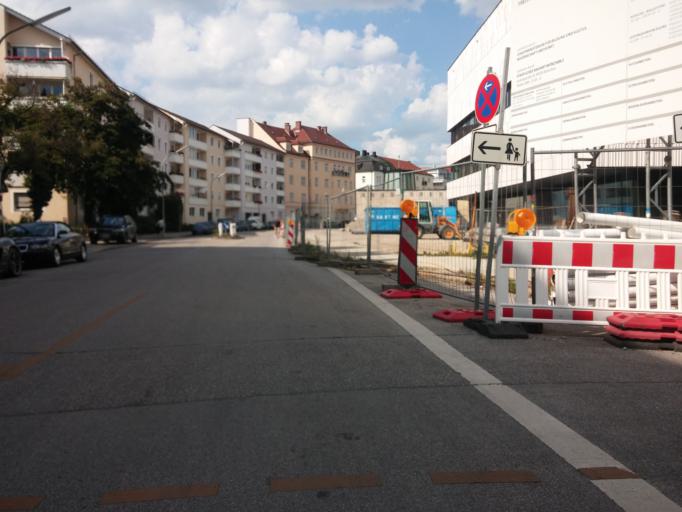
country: DE
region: Bavaria
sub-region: Upper Bavaria
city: Munich
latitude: 48.1513
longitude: 11.5852
